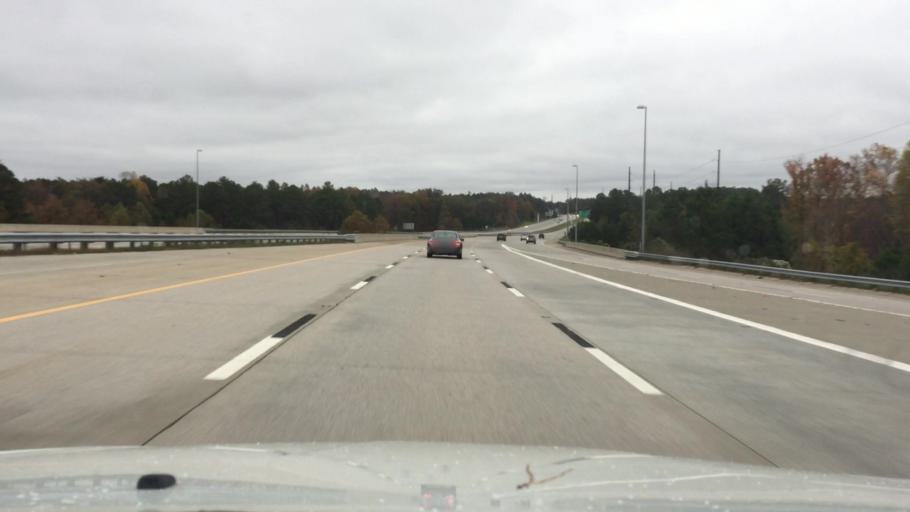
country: US
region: North Carolina
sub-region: Wake County
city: Morrisville
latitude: 35.8432
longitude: -78.8822
